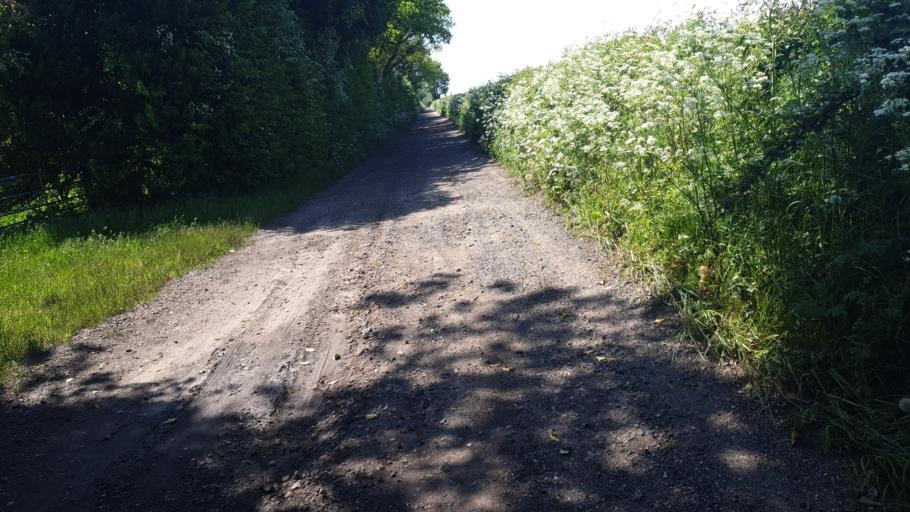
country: GB
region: England
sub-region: Essex
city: Manningtree
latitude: 51.9335
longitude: 1.0411
